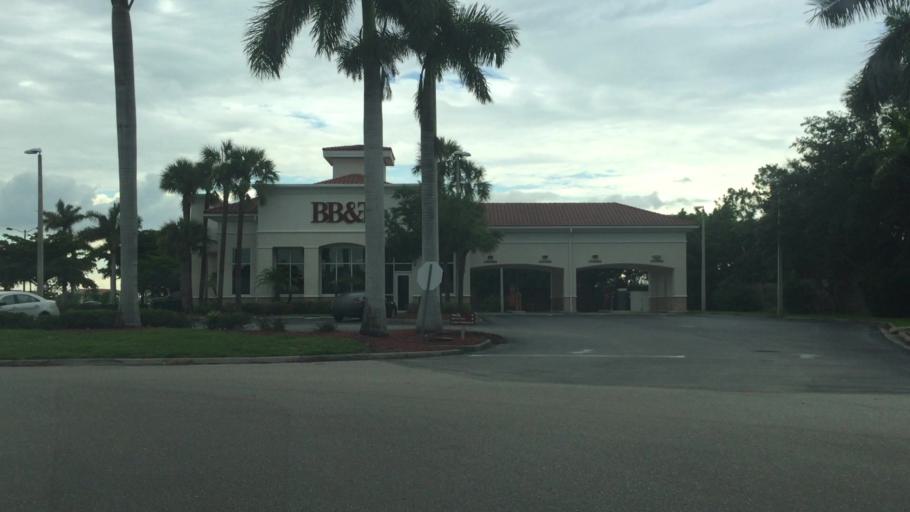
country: US
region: Florida
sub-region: Lee County
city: Estero
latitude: 26.4394
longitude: -81.7705
